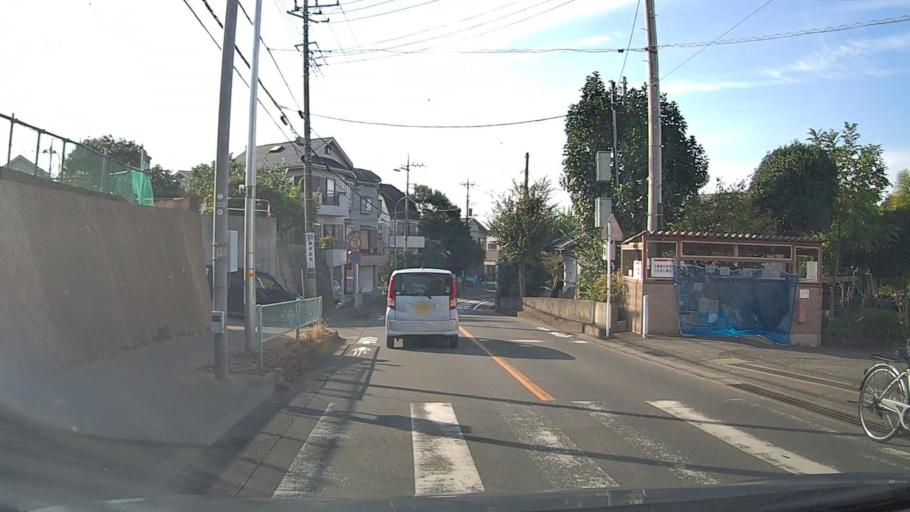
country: JP
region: Tokyo
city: Tanashicho
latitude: 35.7605
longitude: 139.5536
